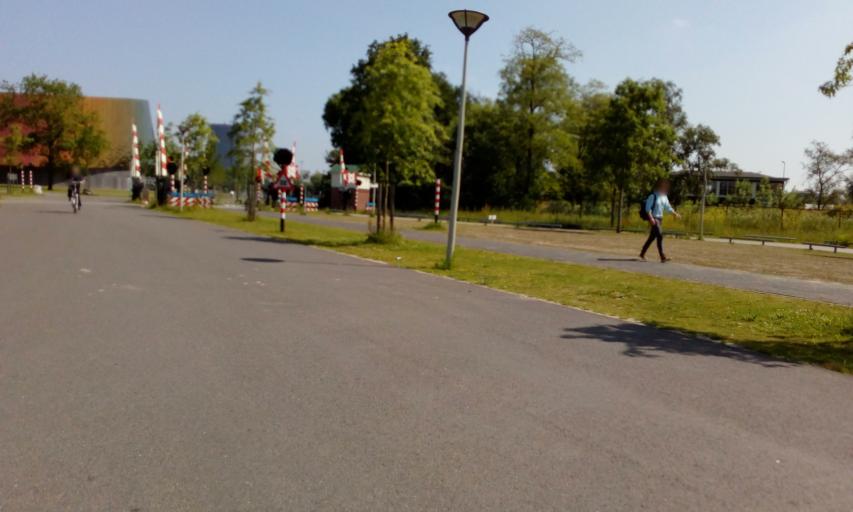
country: NL
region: South Holland
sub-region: Gemeente Den Haag
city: The Hague
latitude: 52.0541
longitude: 4.2890
